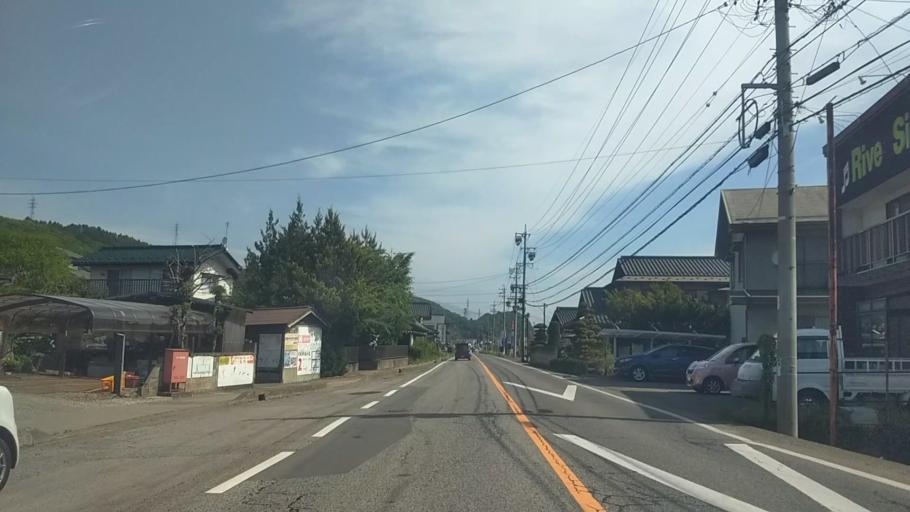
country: JP
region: Nagano
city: Saku
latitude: 36.1449
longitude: 138.4734
